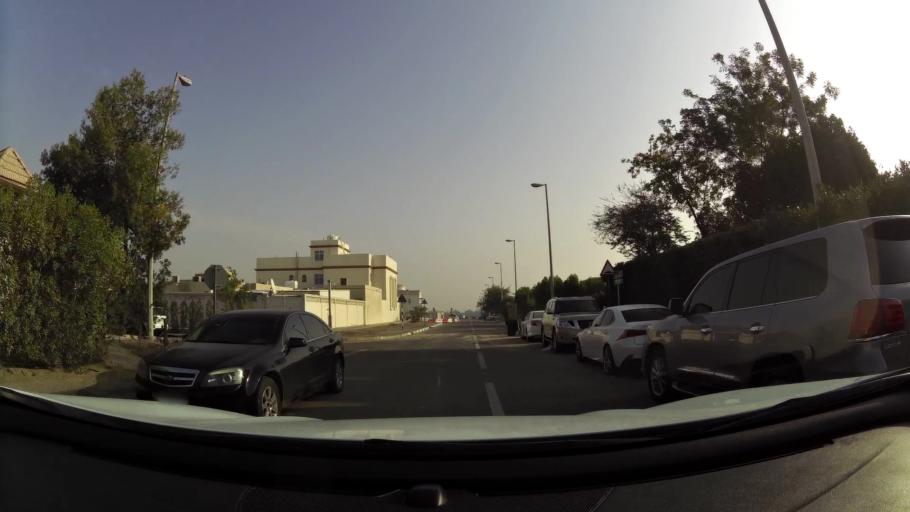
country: AE
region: Abu Dhabi
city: Abu Dhabi
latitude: 24.2741
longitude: 54.6481
